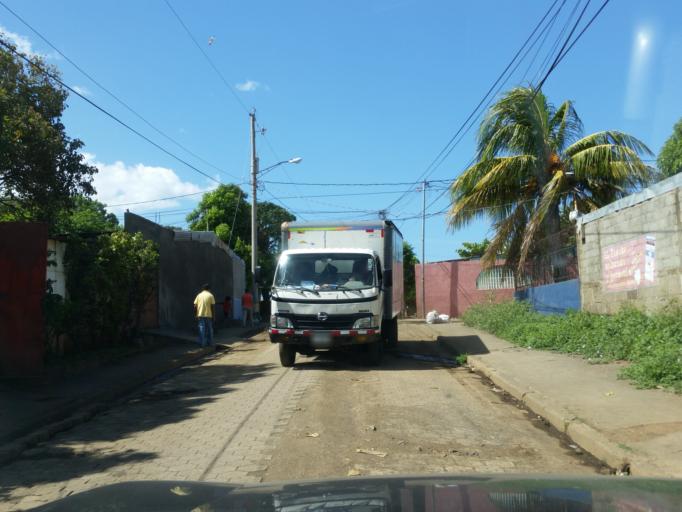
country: NI
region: Managua
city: Managua
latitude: 12.1201
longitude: -86.2284
